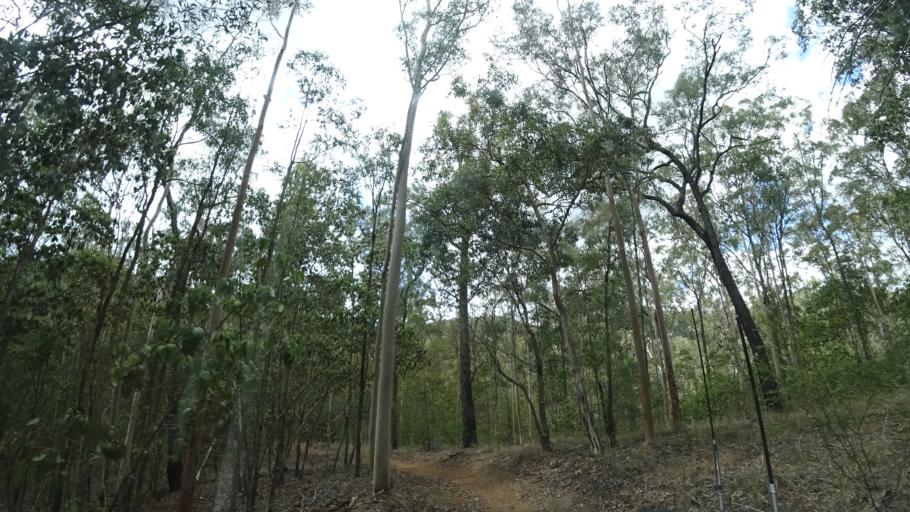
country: AU
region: Queensland
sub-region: Moreton Bay
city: Highvale
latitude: -27.4140
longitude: 152.7359
